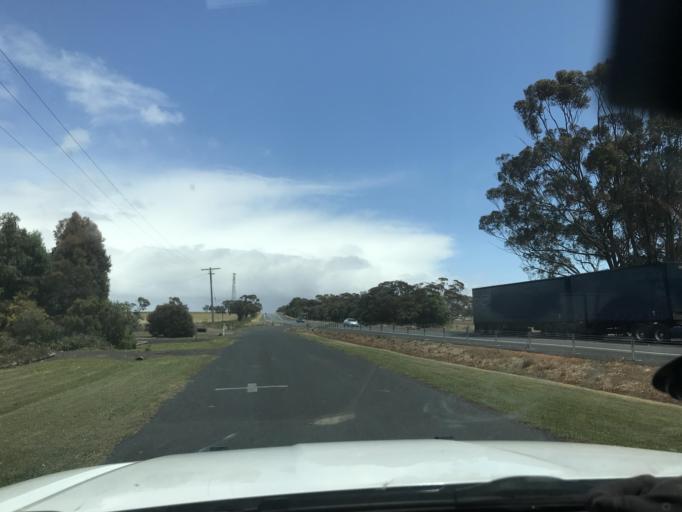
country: AU
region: South Australia
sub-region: Tatiara
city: Bordertown
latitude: -36.3619
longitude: 141.1249
